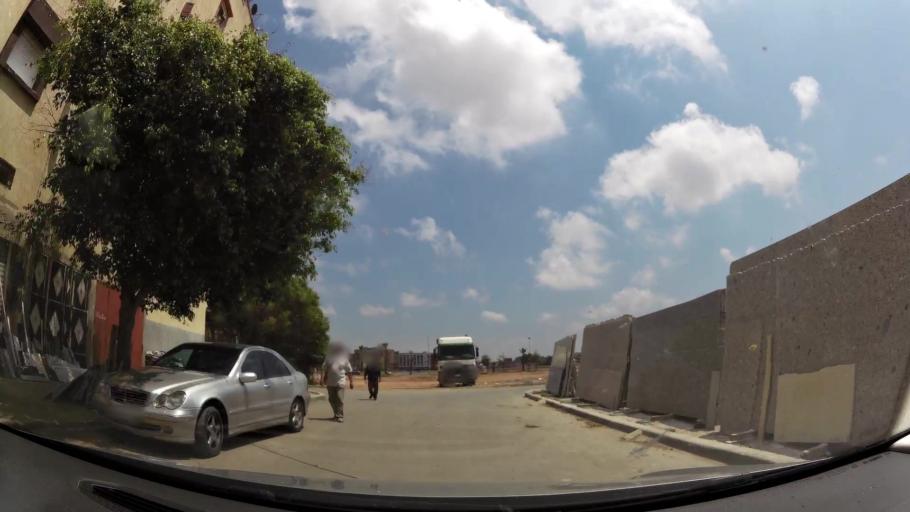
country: MA
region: Rabat-Sale-Zemmour-Zaer
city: Sale
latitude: 34.0580
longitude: -6.7901
